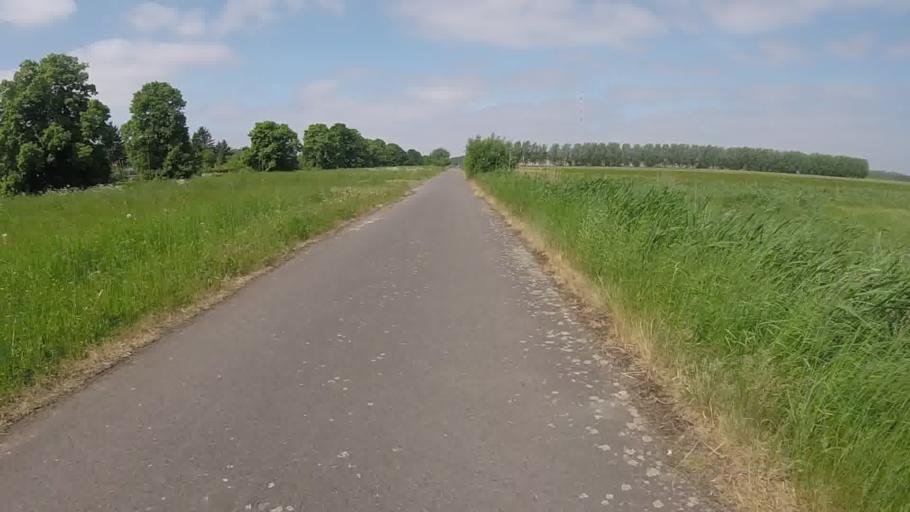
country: DE
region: Hamburg
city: Wandsbek
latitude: 53.5064
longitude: 10.1175
